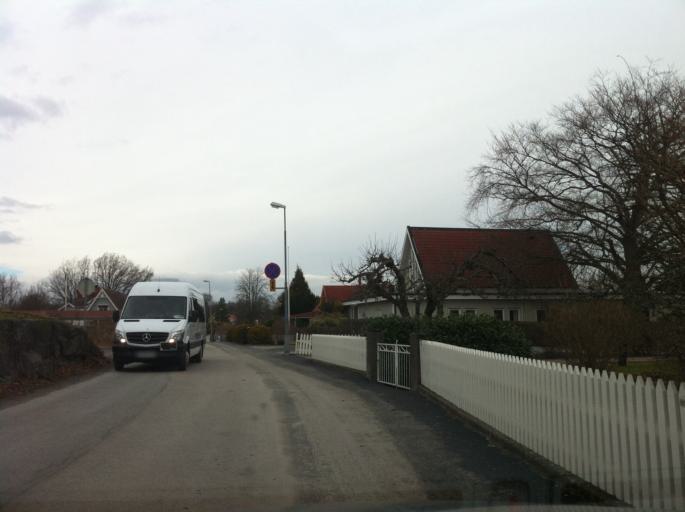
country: SE
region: Blekinge
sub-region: Karlshamns Kommun
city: Karlshamn
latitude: 56.1911
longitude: 14.8963
